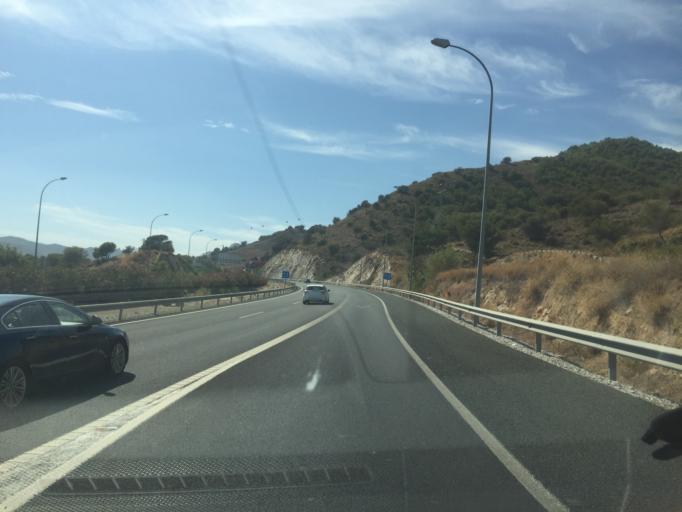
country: ES
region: Andalusia
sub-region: Provincia de Malaga
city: Nerja
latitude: 36.7632
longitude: -3.8542
